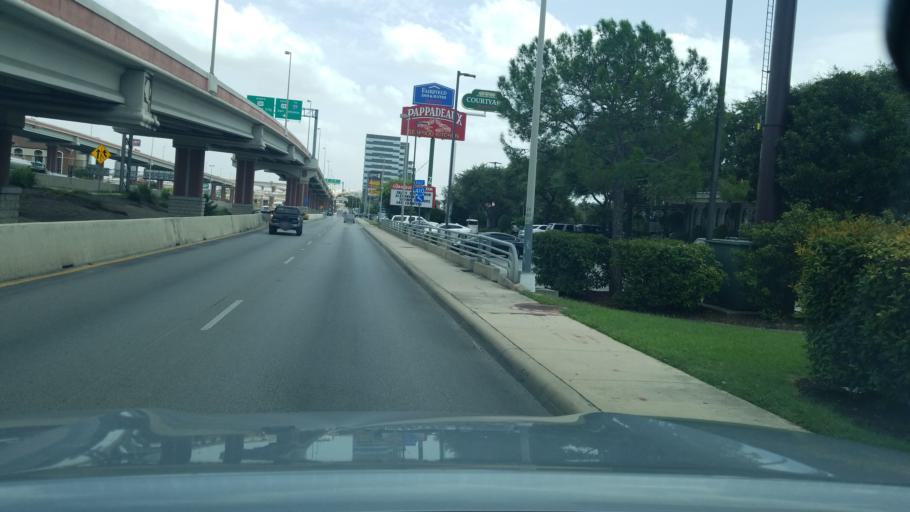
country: US
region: Texas
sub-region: Bexar County
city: Castle Hills
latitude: 29.5200
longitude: -98.4887
